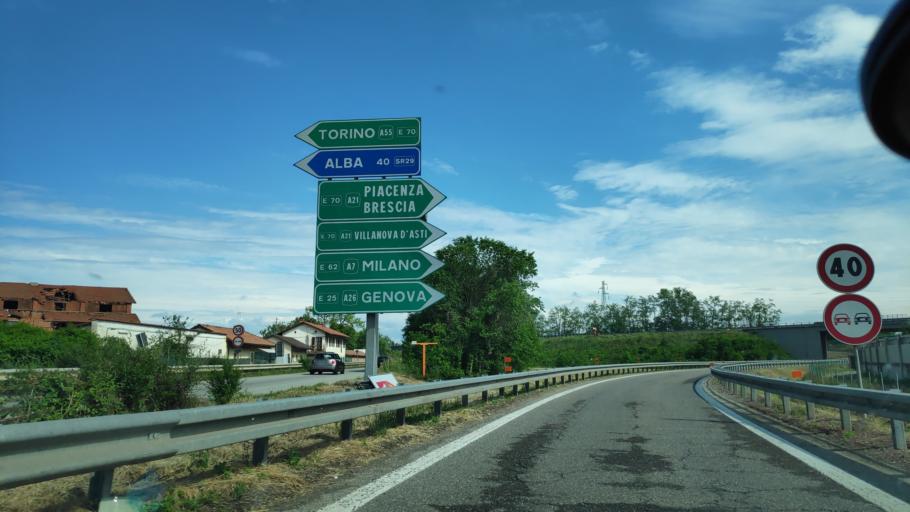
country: IT
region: Piedmont
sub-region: Provincia di Torino
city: Cambiano
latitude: 44.9615
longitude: 7.7798
